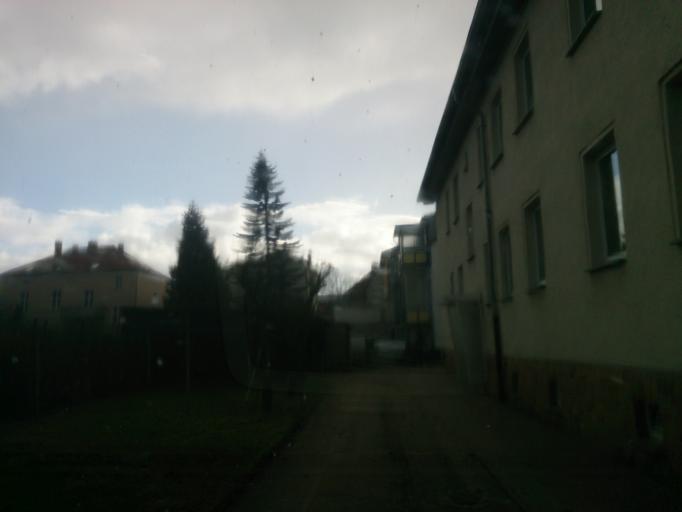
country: DE
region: Mecklenburg-Vorpommern
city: Waren
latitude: 53.5212
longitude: 12.6824
